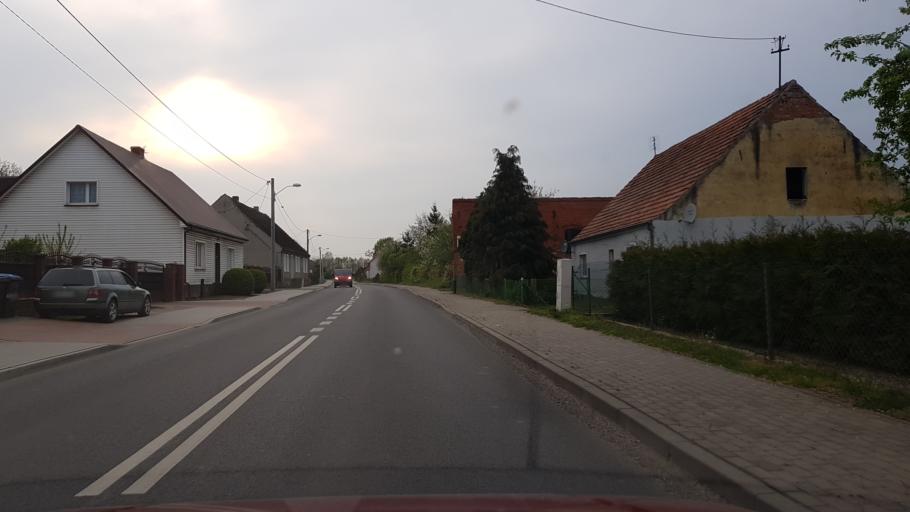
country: PL
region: West Pomeranian Voivodeship
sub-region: Powiat pyrzycki
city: Bielice
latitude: 53.2744
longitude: 14.6704
